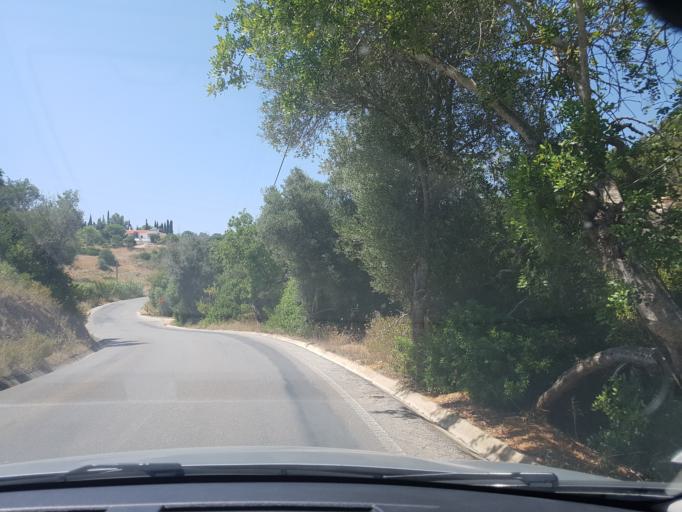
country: PT
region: Faro
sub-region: Lagoa
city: Carvoeiro
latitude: 37.1013
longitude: -8.4267
